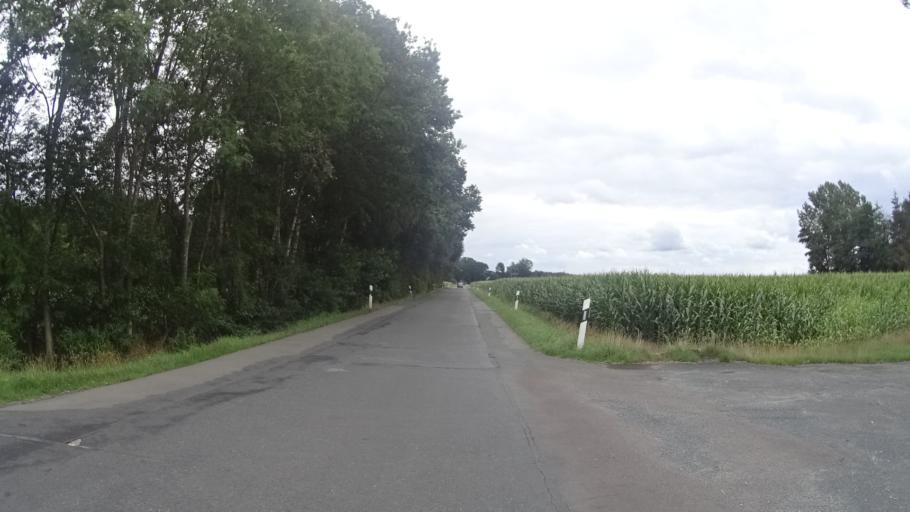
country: DE
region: Lower Saxony
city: Stinstedt
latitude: 53.6391
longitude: 8.9505
